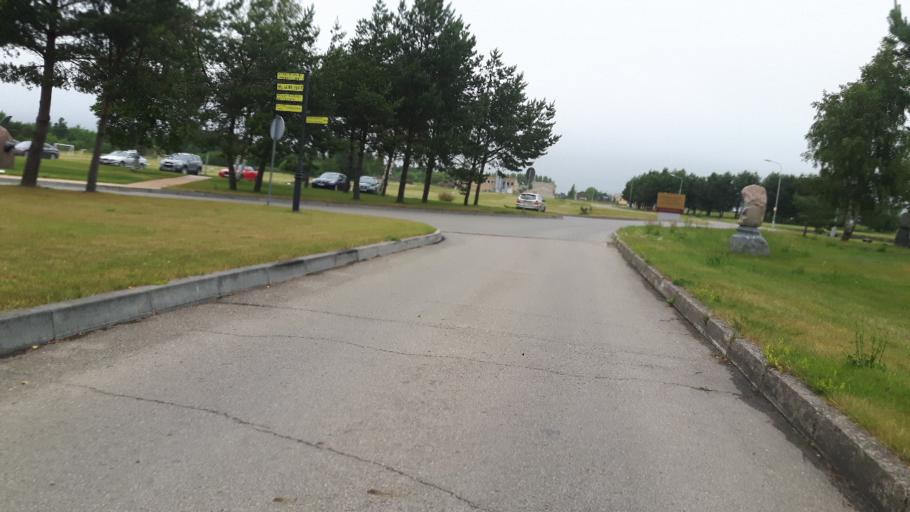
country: LT
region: Klaipedos apskritis
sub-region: Palanga
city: Sventoji
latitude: 56.0386
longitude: 21.0773
